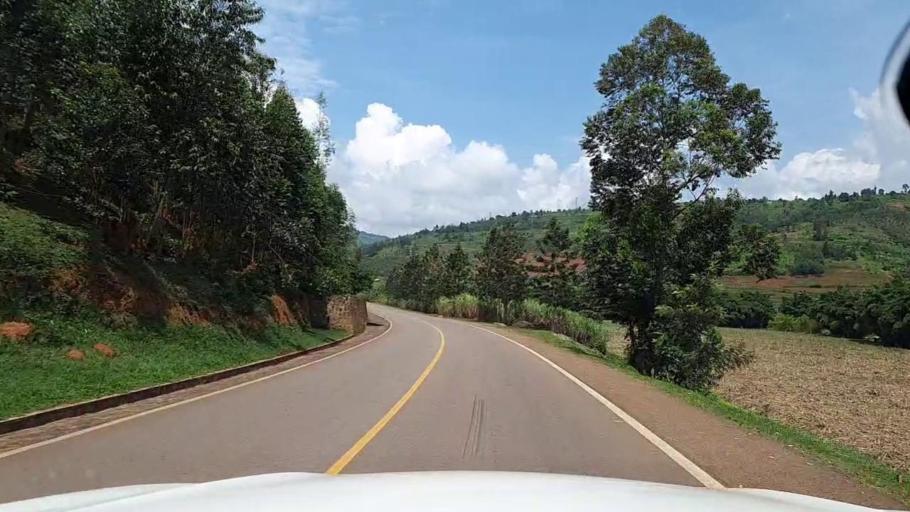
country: RW
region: Kigali
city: Kigali
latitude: -1.8452
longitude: 30.0944
